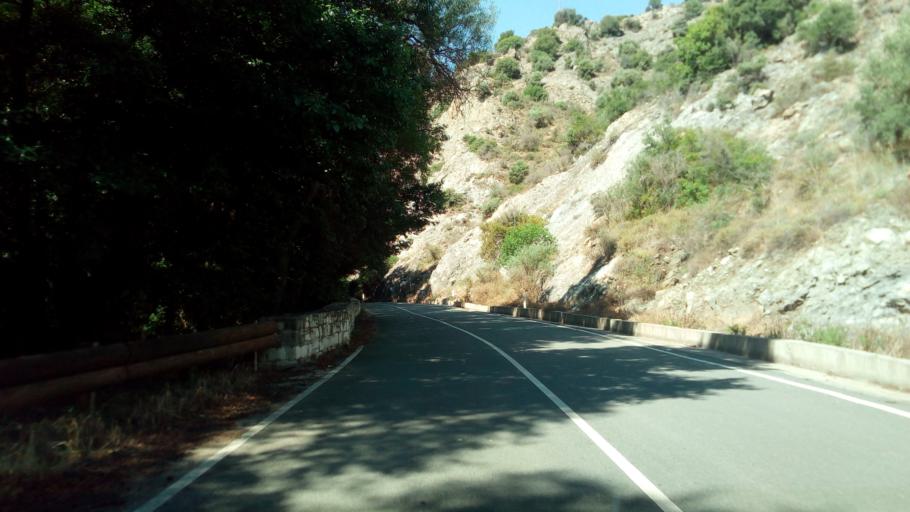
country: CY
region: Limassol
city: Pachna
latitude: 34.7999
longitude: 32.7064
